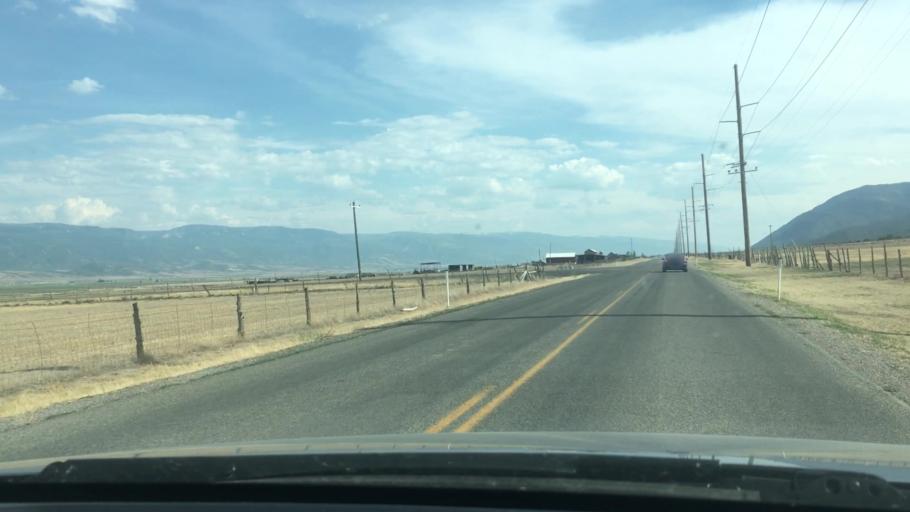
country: US
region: Utah
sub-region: Sanpete County
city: Moroni
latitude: 39.5243
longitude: -111.6397
